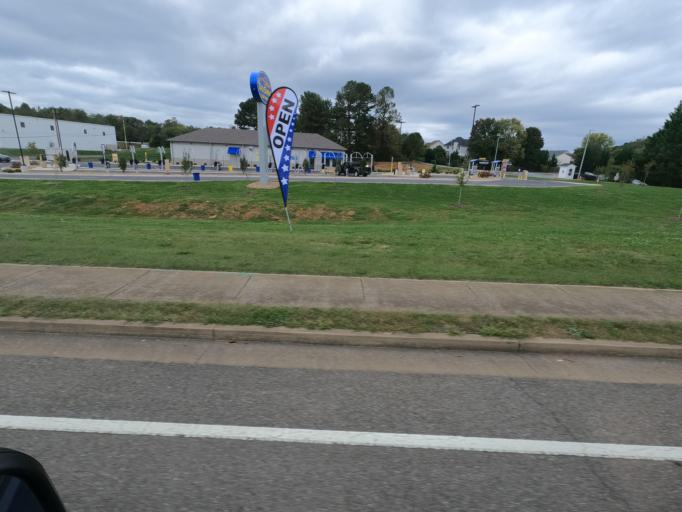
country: US
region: Tennessee
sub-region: Washington County
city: Oak Grove
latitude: 36.3853
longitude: -82.4165
